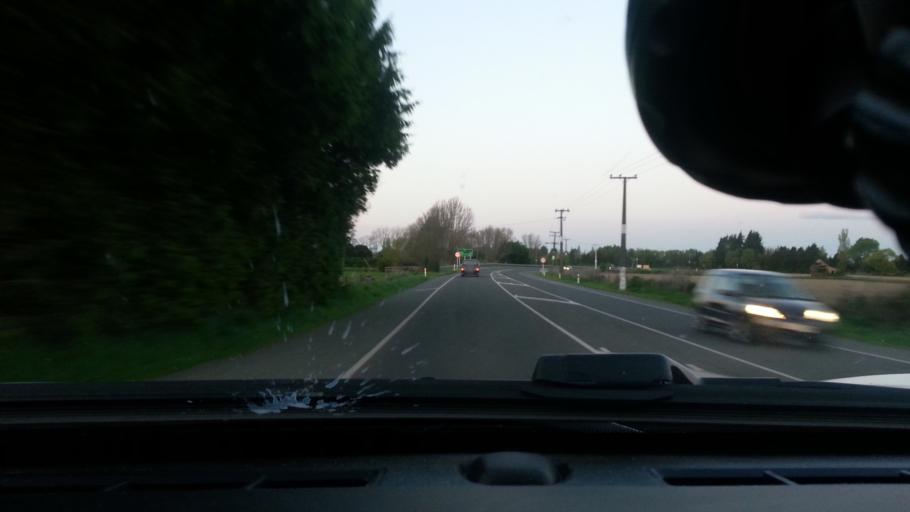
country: NZ
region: Wellington
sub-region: Masterton District
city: Masterton
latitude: -41.0696
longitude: 175.4723
